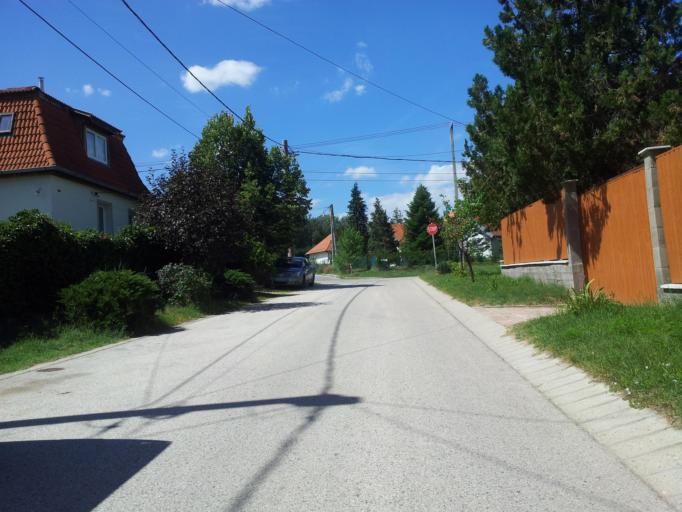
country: HU
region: Pest
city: Veresegyhaz
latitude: 47.6512
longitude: 19.2715
